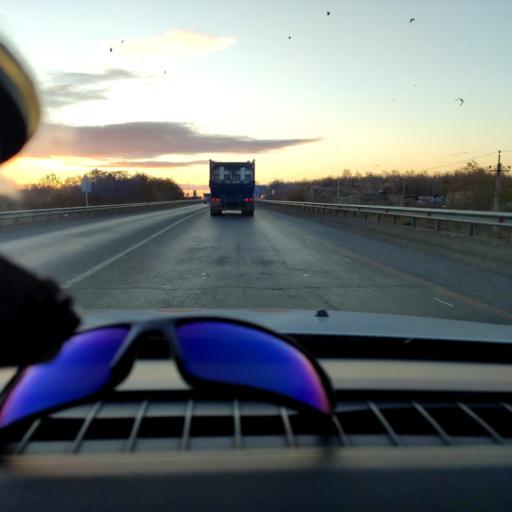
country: RU
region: Samara
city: Novokuybyshevsk
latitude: 53.0842
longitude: 50.0676
